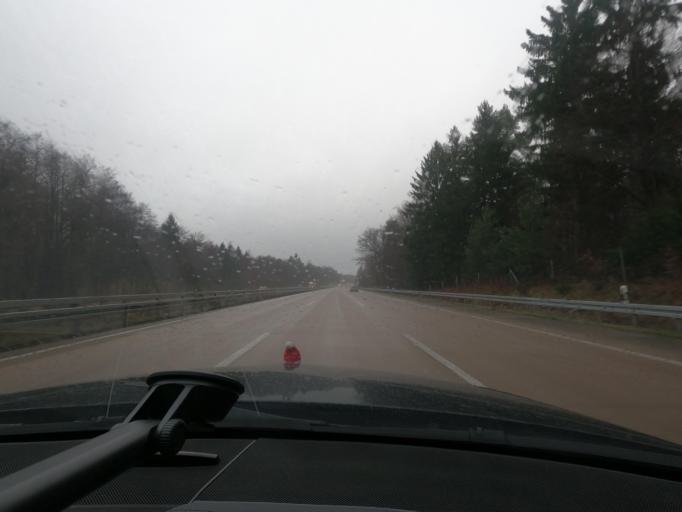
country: DE
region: Lower Saxony
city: Egestorf
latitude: 53.2173
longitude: 10.0766
